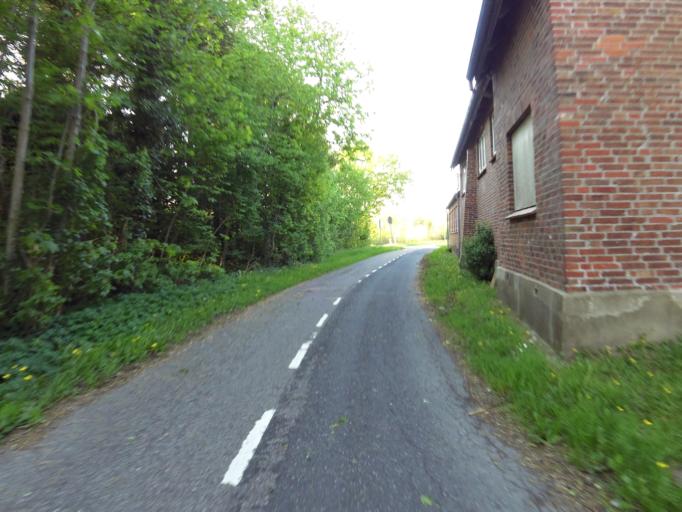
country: DK
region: South Denmark
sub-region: Esbjerg Kommune
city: Ribe
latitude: 55.2887
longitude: 8.7356
